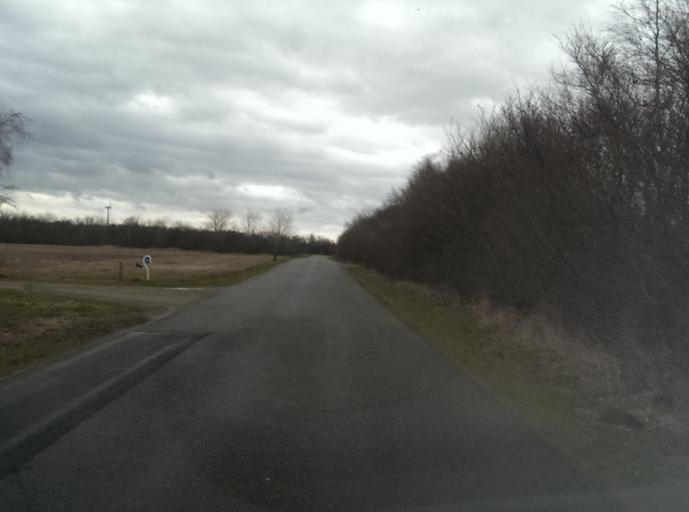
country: DK
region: Central Jutland
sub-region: Ringkobing-Skjern Kommune
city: Ringkobing
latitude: 56.1279
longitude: 8.3231
